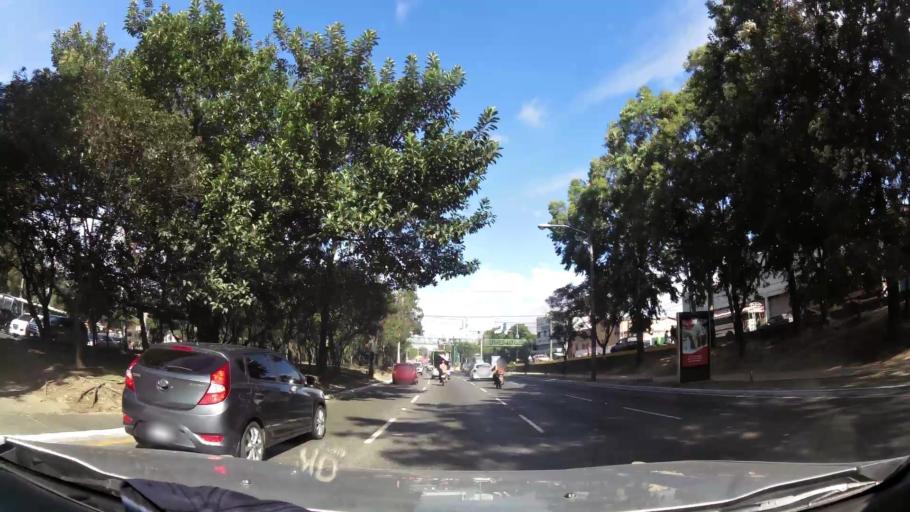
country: GT
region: Guatemala
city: Guatemala City
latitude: 14.6100
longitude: -90.5322
